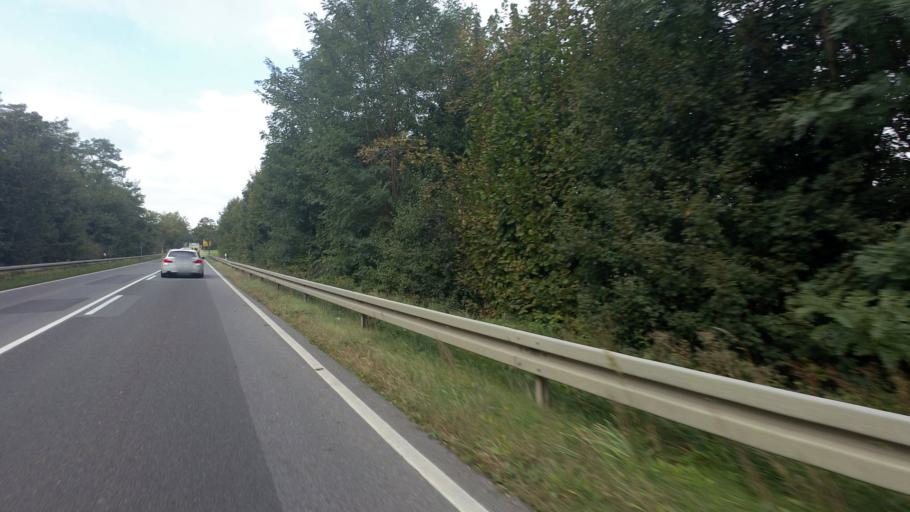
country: DE
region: Brandenburg
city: Lauchhammer
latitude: 51.4651
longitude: 13.7844
